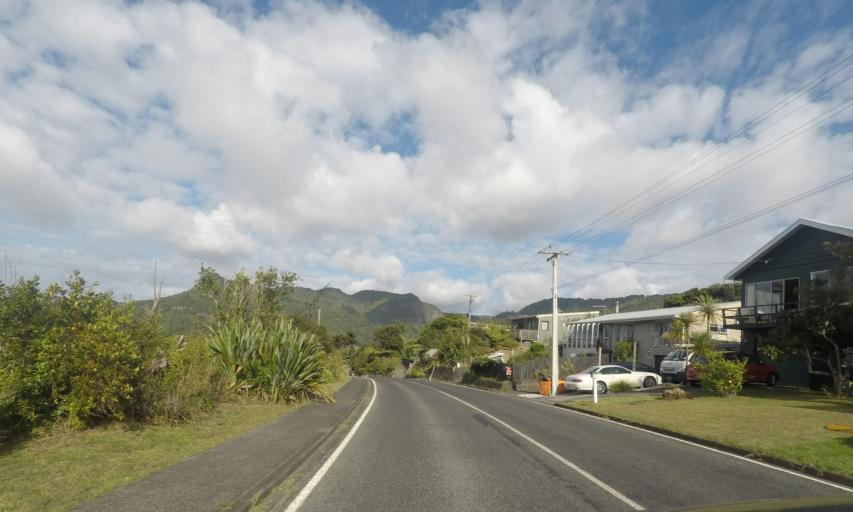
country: NZ
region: Auckland
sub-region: Auckland
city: Titirangi
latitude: -37.0029
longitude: 174.5758
